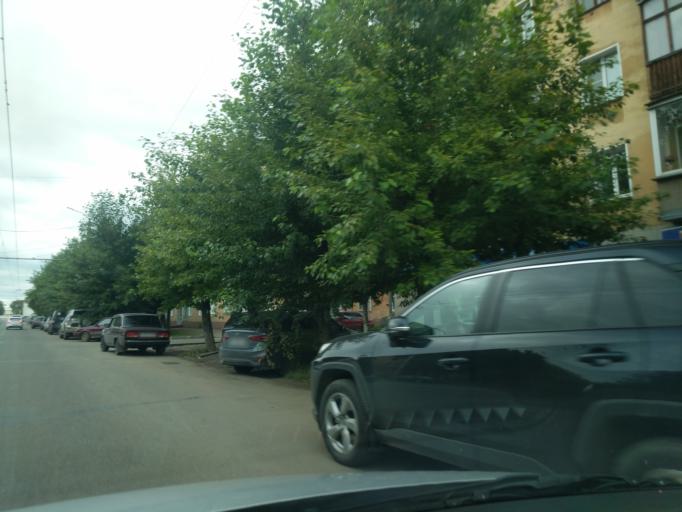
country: RU
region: Kirov
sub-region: Kirovo-Chepetskiy Rayon
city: Kirov
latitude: 58.6379
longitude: 49.6170
